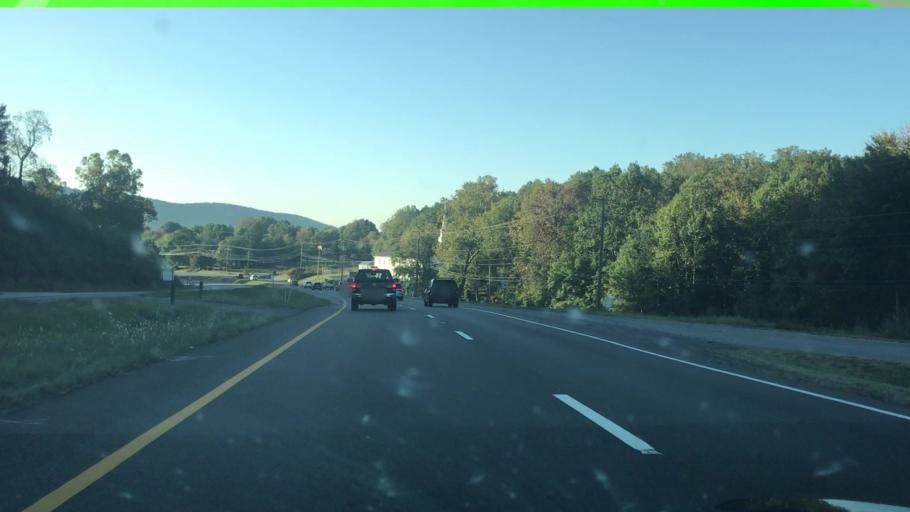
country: US
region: Virginia
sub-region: Botetourt County
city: Cloverdale
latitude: 37.3473
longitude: -79.8828
